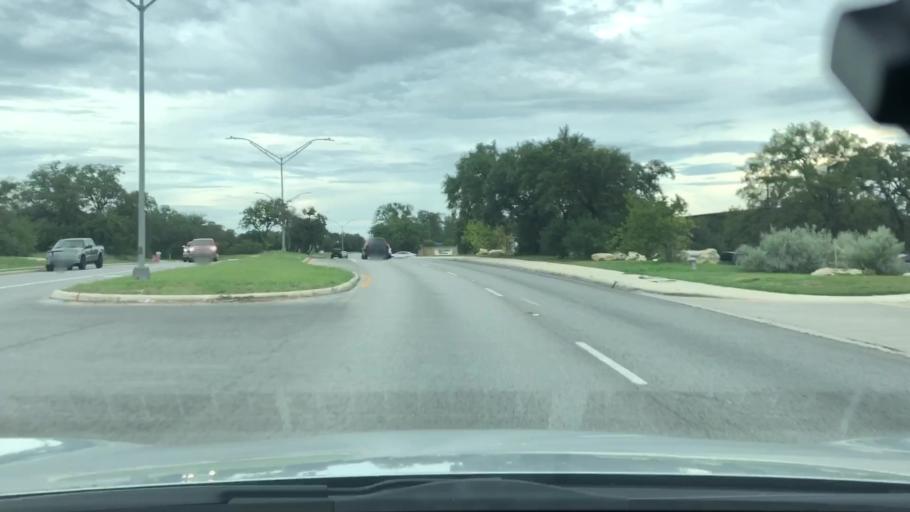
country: US
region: Texas
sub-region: Bexar County
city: Leon Valley
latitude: 29.4692
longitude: -98.6754
